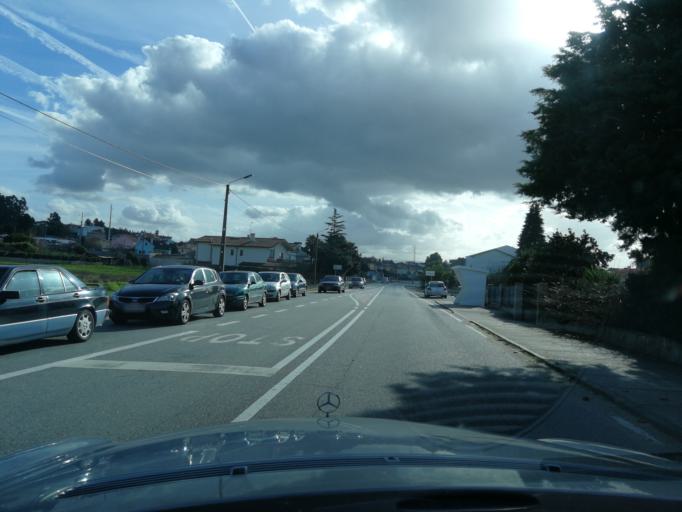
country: PT
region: Viana do Castelo
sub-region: Valenca
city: Valenza
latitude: 42.0329
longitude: -8.6296
